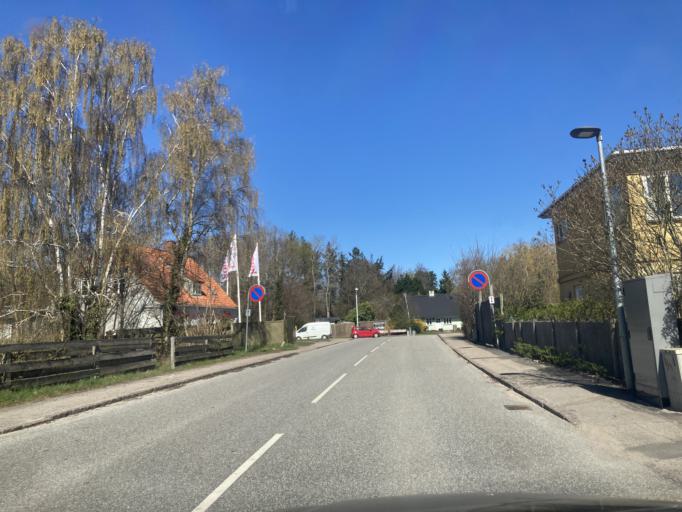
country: DK
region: Capital Region
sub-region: Gribskov Kommune
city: Graested
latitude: 56.1148
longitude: 12.2367
